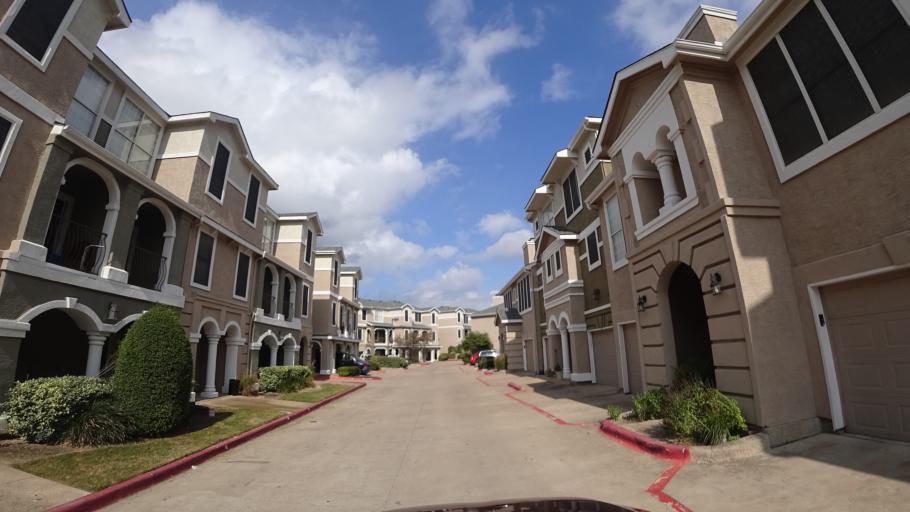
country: US
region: Texas
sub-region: Travis County
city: Hudson Bend
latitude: 30.3837
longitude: -97.8811
